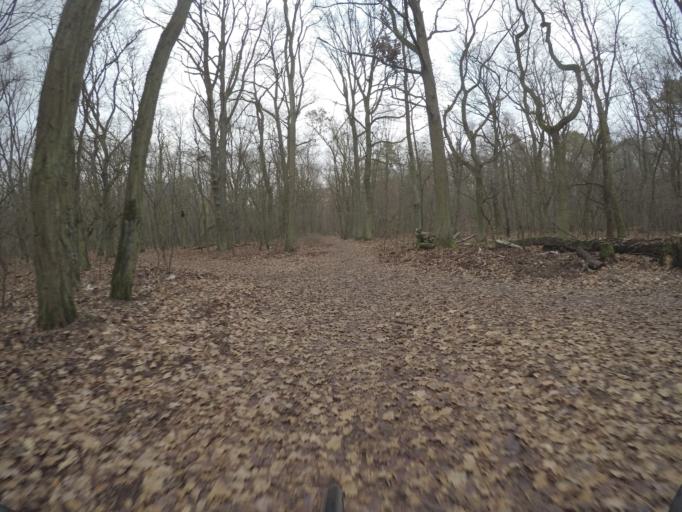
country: DE
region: Berlin
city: Grunau
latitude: 52.4160
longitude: 13.5977
